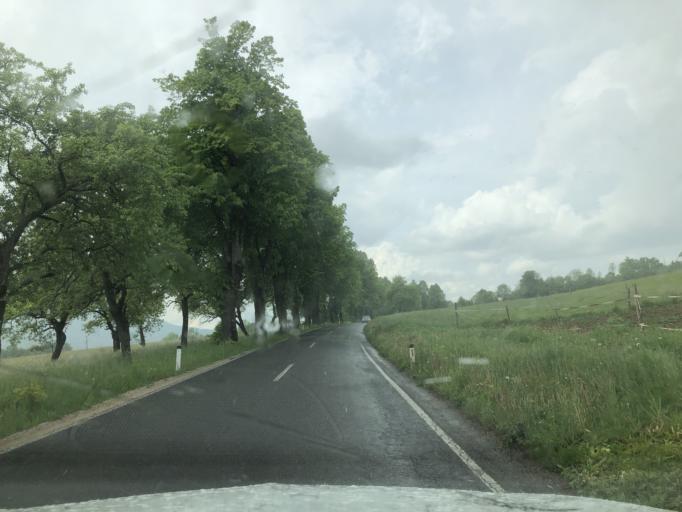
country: SI
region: Cerknica
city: Cerknica
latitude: 45.7787
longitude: 14.3955
